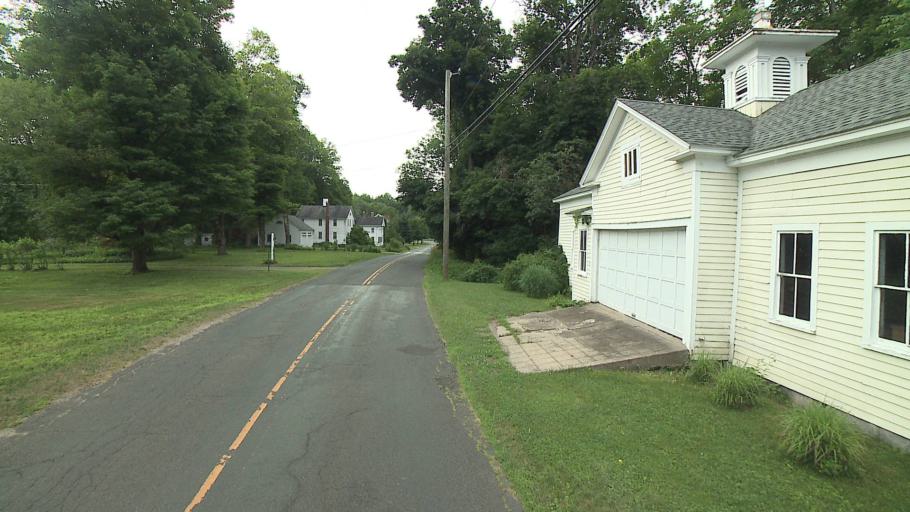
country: US
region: Connecticut
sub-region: Litchfield County
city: New Hartford Center
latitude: 41.9153
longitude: -72.9874
